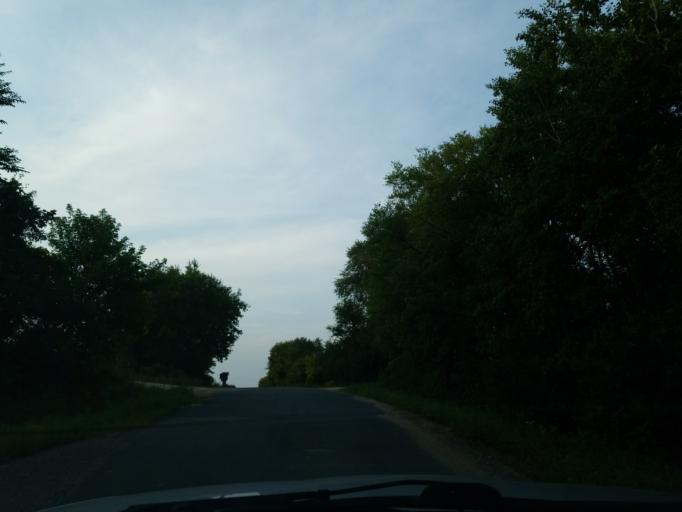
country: US
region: Minnesota
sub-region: Washington County
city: Oak Park Heights
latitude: 45.0640
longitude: -92.7610
